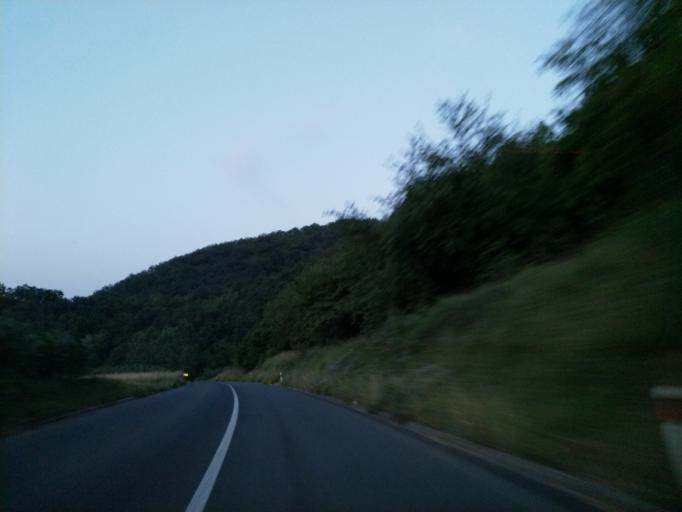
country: RS
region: Central Serbia
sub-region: Rasinski Okrug
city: Aleksandrovac
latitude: 43.3421
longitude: 21.1118
